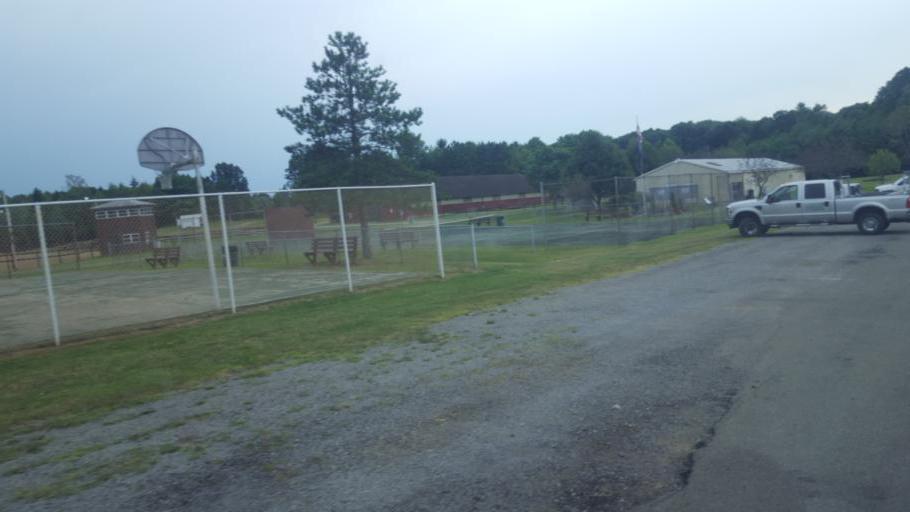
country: US
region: Pennsylvania
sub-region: Clarion County
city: Marianne
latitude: 41.2021
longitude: -79.4360
